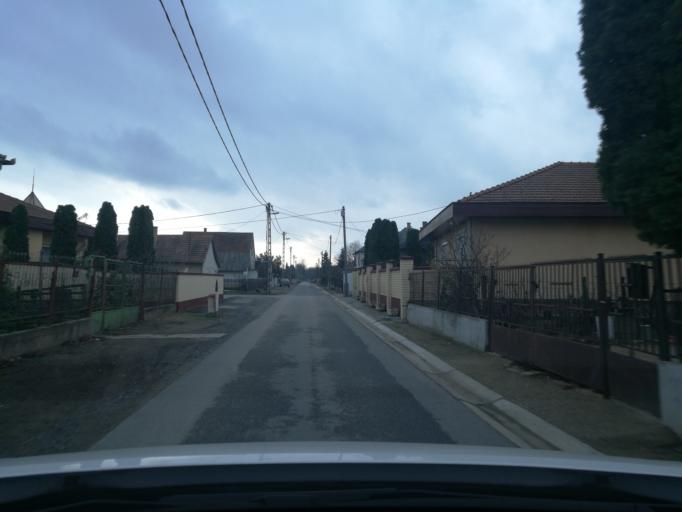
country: HU
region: Szabolcs-Szatmar-Bereg
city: Nyirpazony
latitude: 47.9797
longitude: 21.7877
